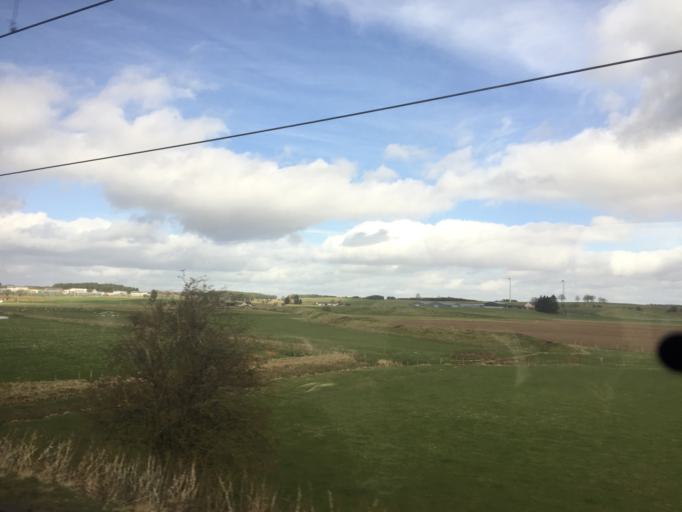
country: GB
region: Scotland
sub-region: South Lanarkshire
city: Carnwath
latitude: 55.6833
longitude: -3.6553
